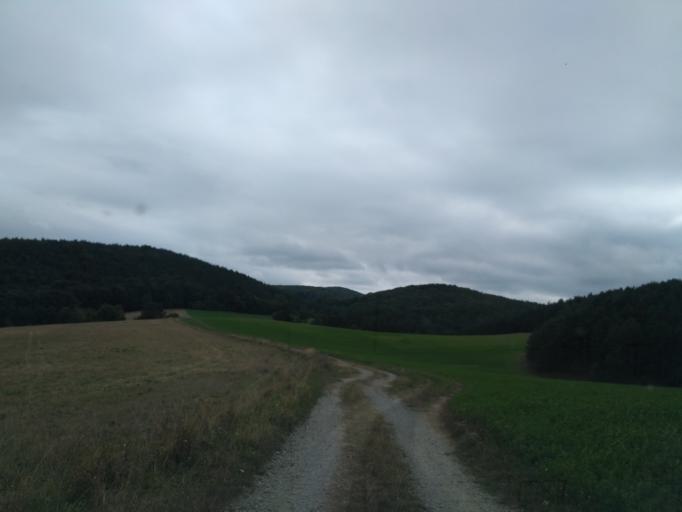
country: SK
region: Presovsky
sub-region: Okres Presov
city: Presov
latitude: 48.9043
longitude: 21.1590
